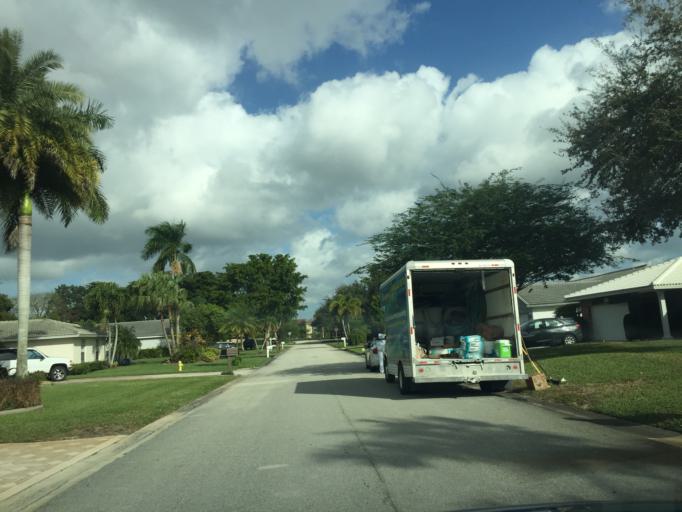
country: US
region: Florida
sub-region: Broward County
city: Tamarac
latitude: 26.2335
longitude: -80.2481
